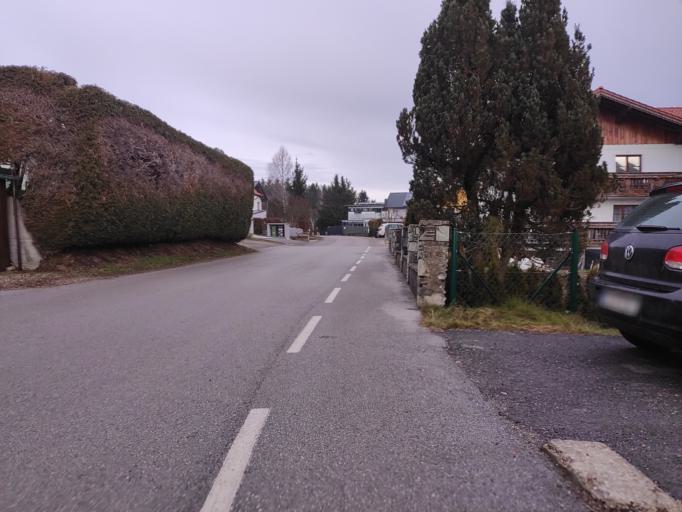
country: AT
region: Salzburg
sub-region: Politischer Bezirk Salzburg-Umgebung
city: Elixhausen
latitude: 47.8954
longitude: 13.0573
